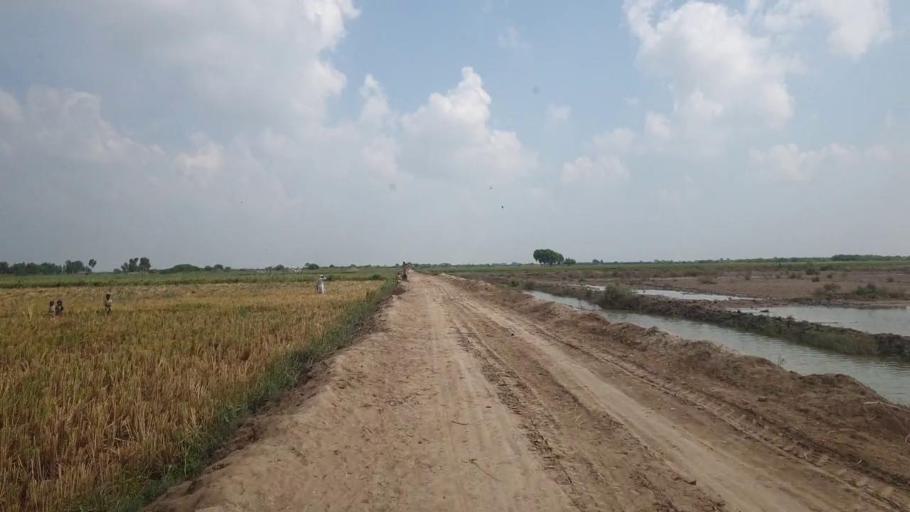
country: PK
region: Sindh
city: Badin
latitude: 24.5328
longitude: 68.6339
